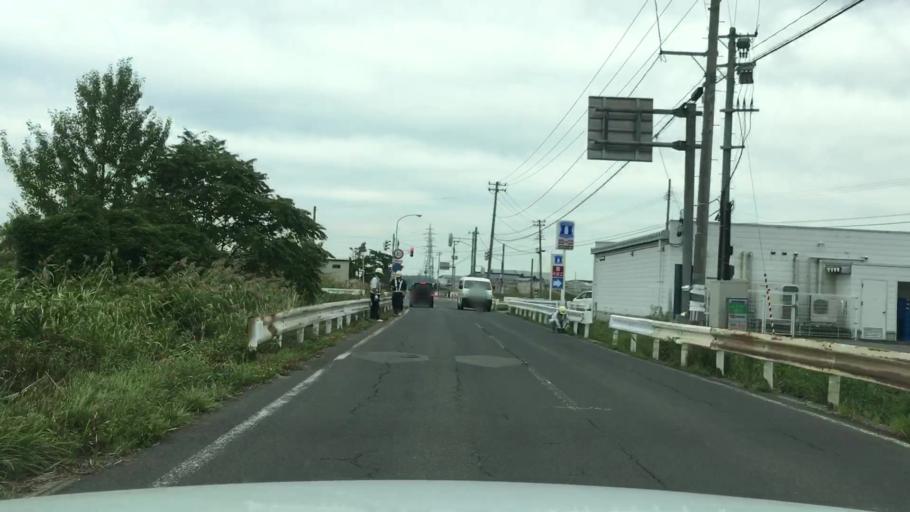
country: JP
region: Aomori
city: Hirosaki
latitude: 40.6304
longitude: 140.4526
